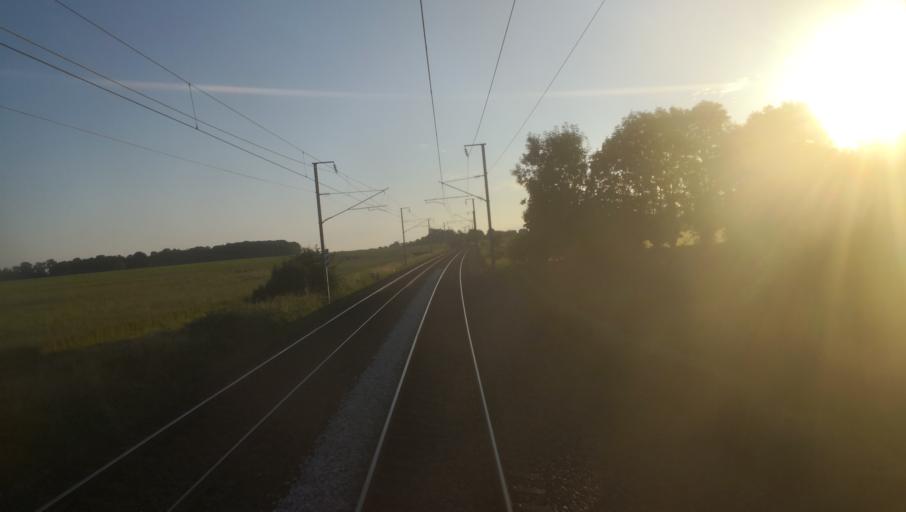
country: FR
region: Haute-Normandie
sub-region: Departement de l'Eure
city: Thiberville
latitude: 49.0810
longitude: 0.5002
